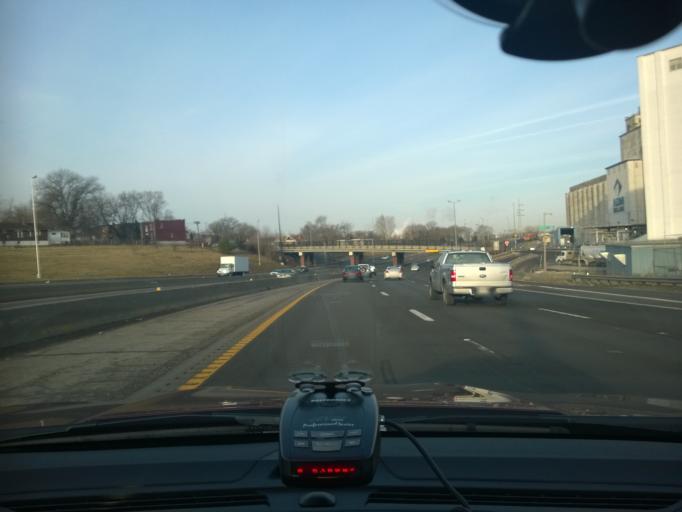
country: US
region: Missouri
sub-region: Saint Louis County
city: Pine Lawn
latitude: 38.6829
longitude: -90.2371
